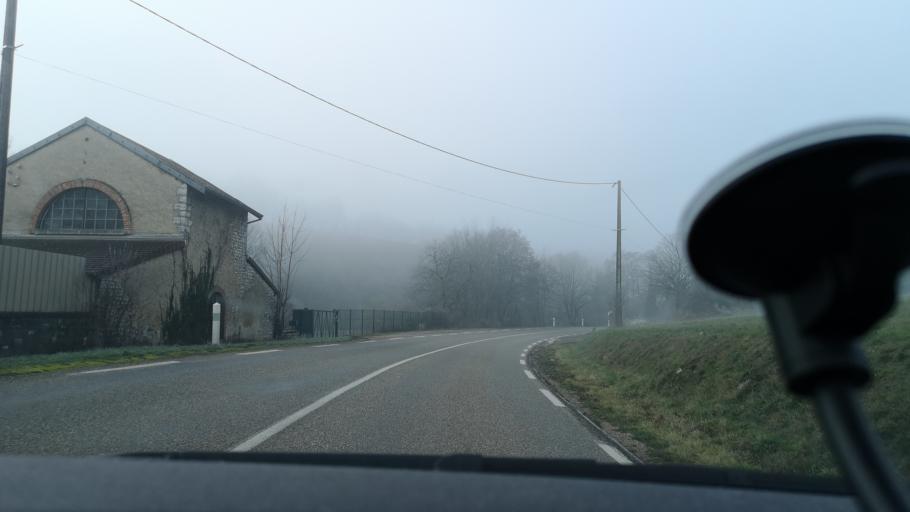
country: FR
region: Franche-Comte
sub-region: Departement du Doubs
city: Clerval
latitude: 47.3638
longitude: 6.4495
